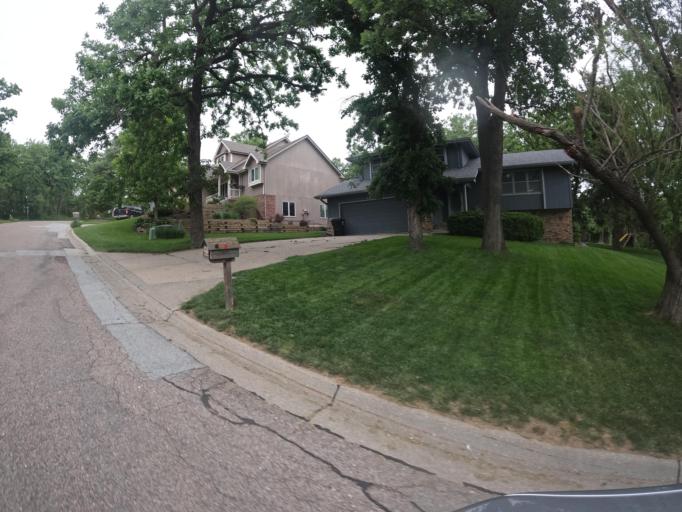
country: US
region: Nebraska
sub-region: Sarpy County
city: Offutt Air Force Base
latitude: 41.0481
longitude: -95.9671
